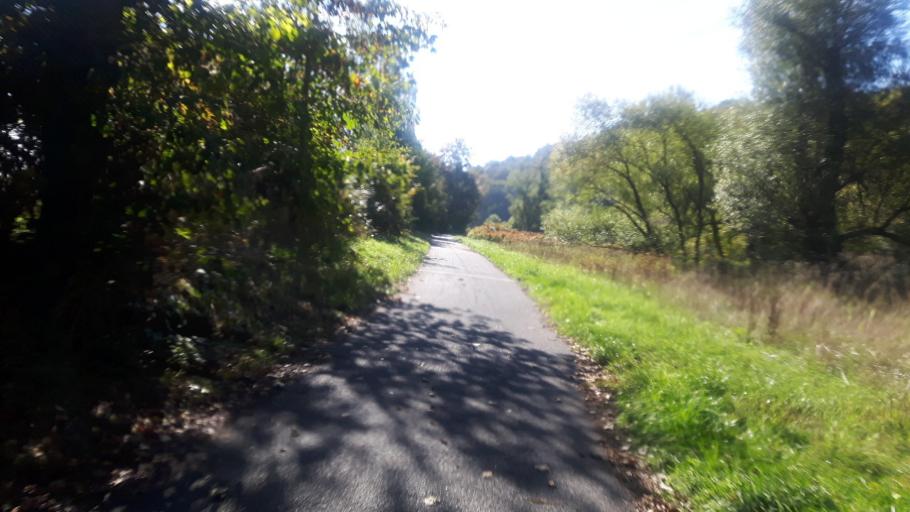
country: DE
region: Rheinland-Pfalz
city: Niederirsen
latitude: 50.7991
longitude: 7.6044
